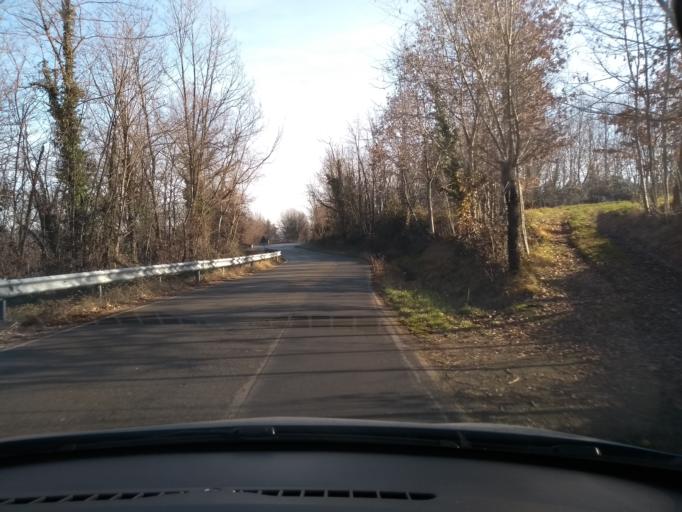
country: IT
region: Piedmont
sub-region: Provincia di Torino
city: Barbania
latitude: 45.2835
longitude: 7.6290
